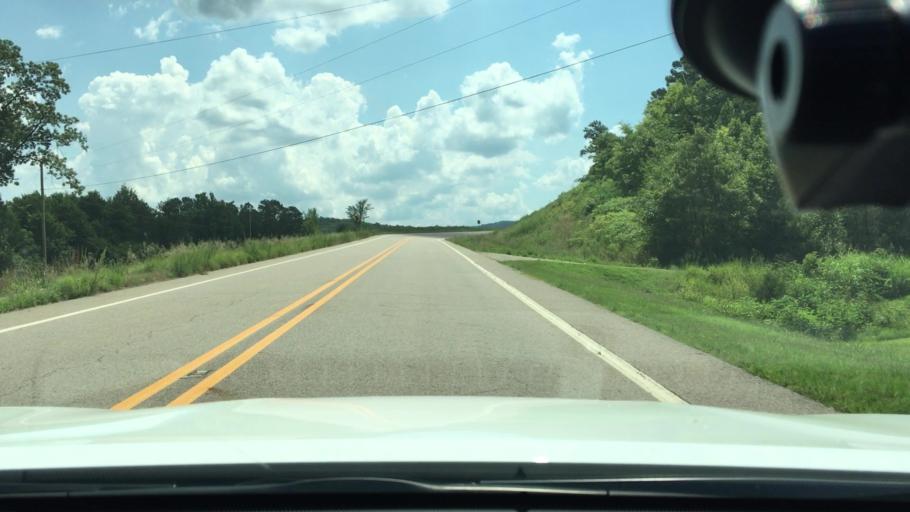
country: US
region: Arkansas
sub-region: Logan County
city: Paris
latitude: 35.2562
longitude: -93.6791
